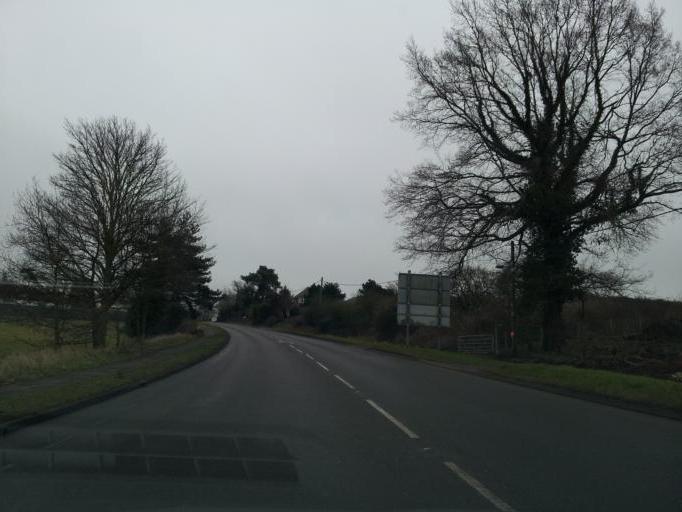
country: GB
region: England
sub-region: Suffolk
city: Shotley Gate
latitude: 51.9273
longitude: 1.2208
